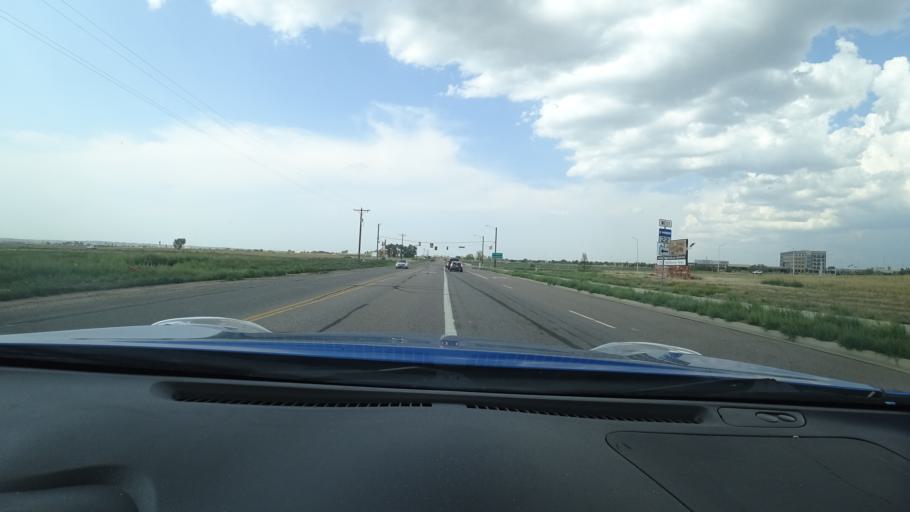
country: US
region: Colorado
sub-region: Adams County
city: Brighton
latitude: 39.9200
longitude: -104.8186
